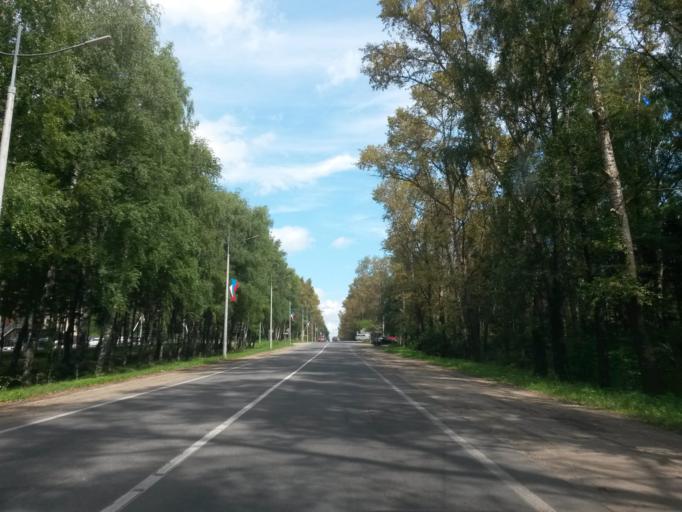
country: RU
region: Jaroslavl
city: Pereslavl'-Zalesskiy
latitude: 56.7514
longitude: 38.8623
